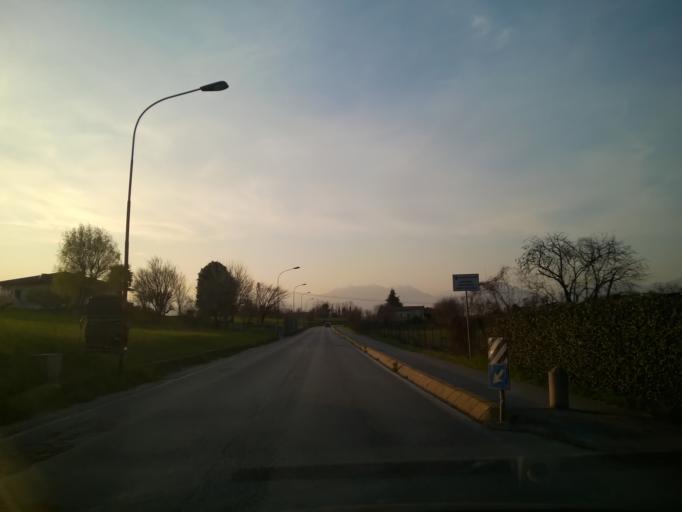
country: IT
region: Veneto
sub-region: Provincia di Vicenza
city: Caldogno-Rettorgole-Cresole
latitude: 45.6250
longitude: 11.5045
